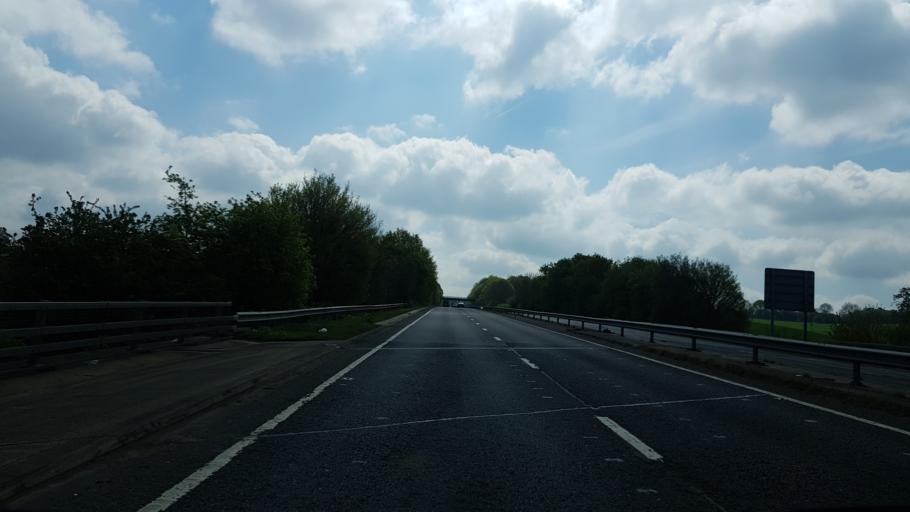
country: GB
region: England
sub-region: Kent
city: Sevenoaks
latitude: 51.2743
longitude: 0.1585
